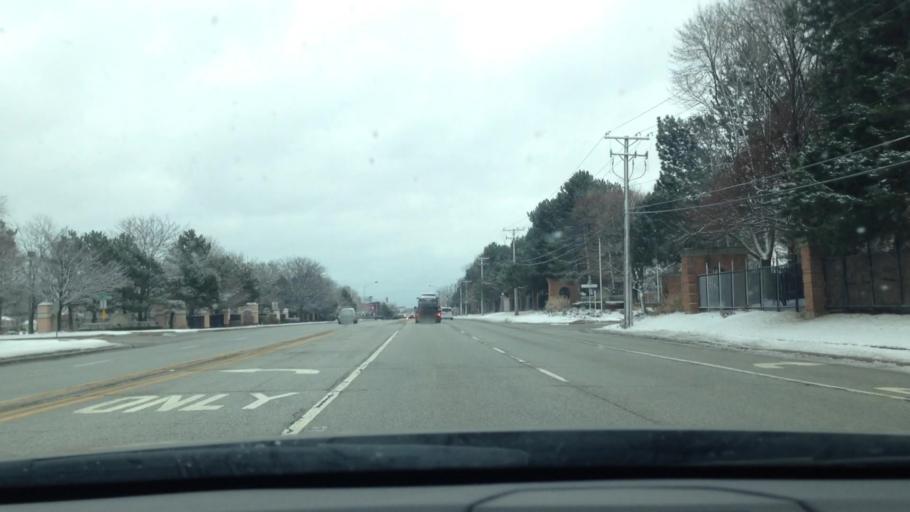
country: US
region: Illinois
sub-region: Cook County
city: Northbrook
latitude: 42.1056
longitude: -87.8337
